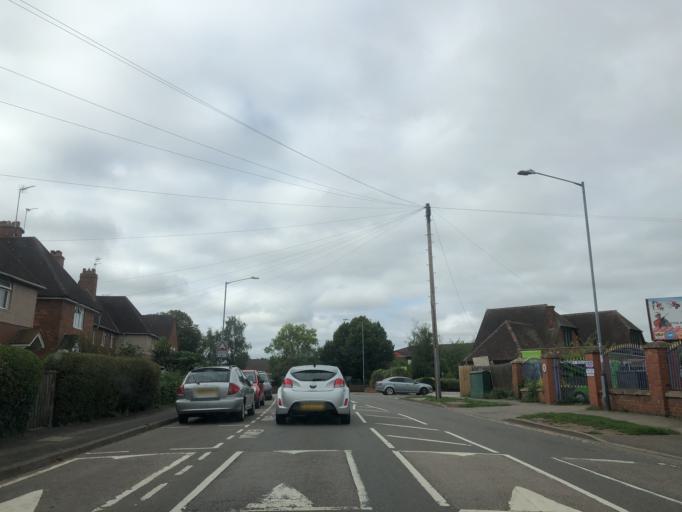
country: GB
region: England
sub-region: Warwickshire
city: Warwick
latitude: 52.2899
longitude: -1.5930
